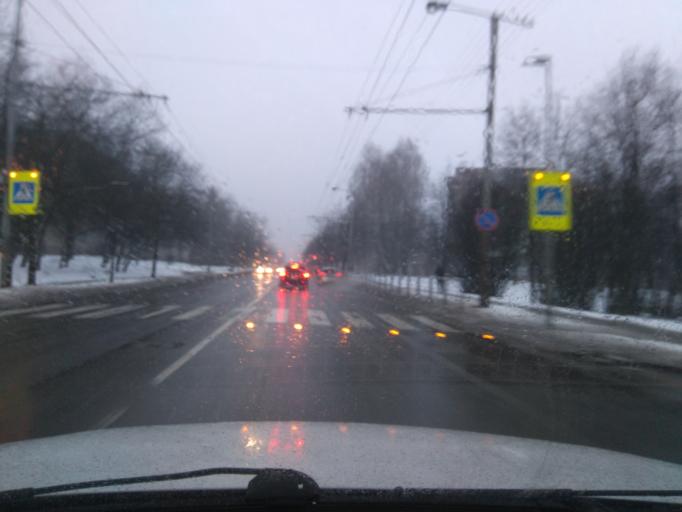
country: LT
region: Kauno apskritis
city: Dainava (Kaunas)
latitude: 54.9073
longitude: 23.9739
